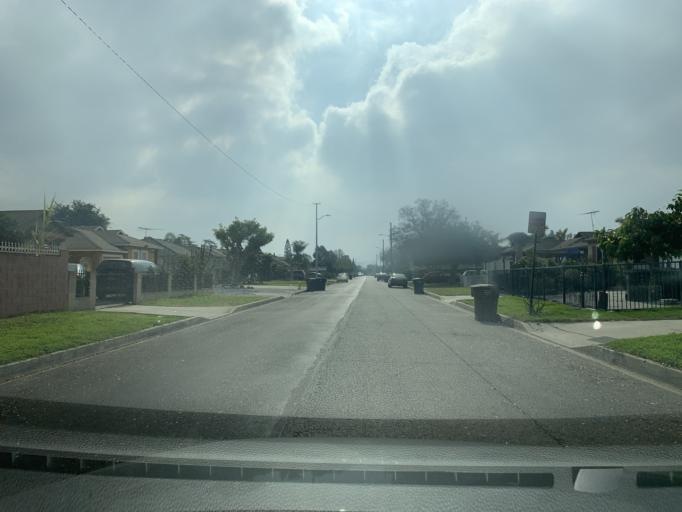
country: US
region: California
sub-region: Los Angeles County
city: South El Monte
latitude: 34.0615
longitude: -118.0459
